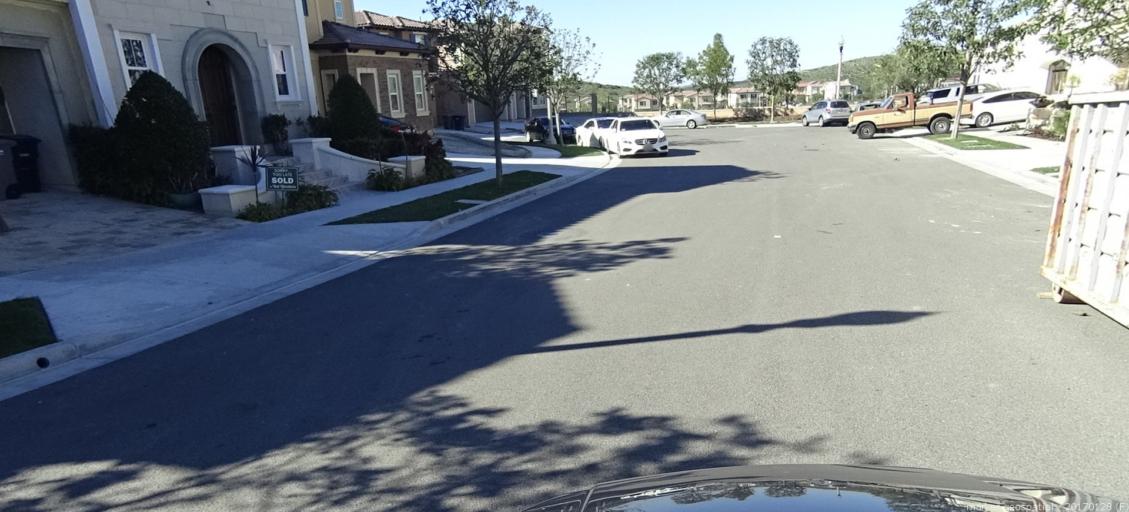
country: US
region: California
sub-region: Orange County
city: Lake Forest
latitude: 33.6714
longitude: -117.6842
